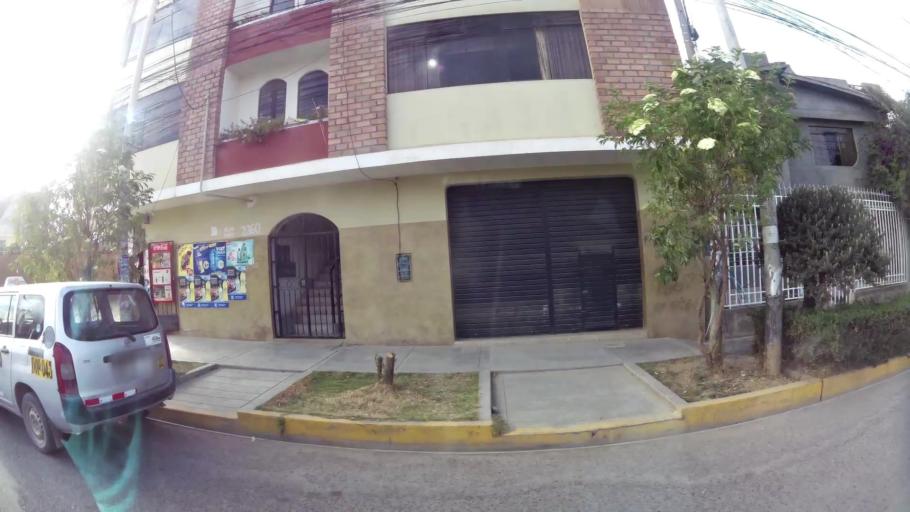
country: PE
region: Junin
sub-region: Provincia de Huancayo
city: Huancayo
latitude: -12.0455
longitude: -75.1980
